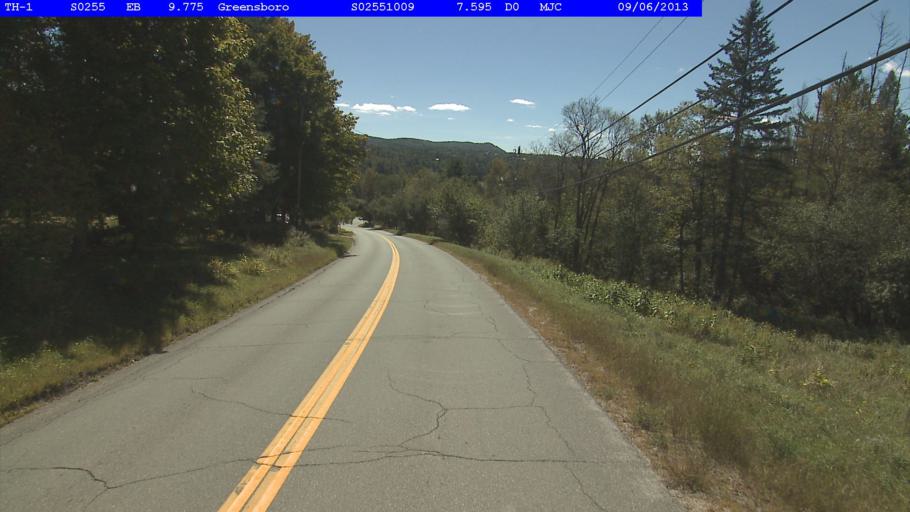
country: US
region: Vermont
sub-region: Caledonia County
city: Hardwick
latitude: 44.5497
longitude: -72.2657
